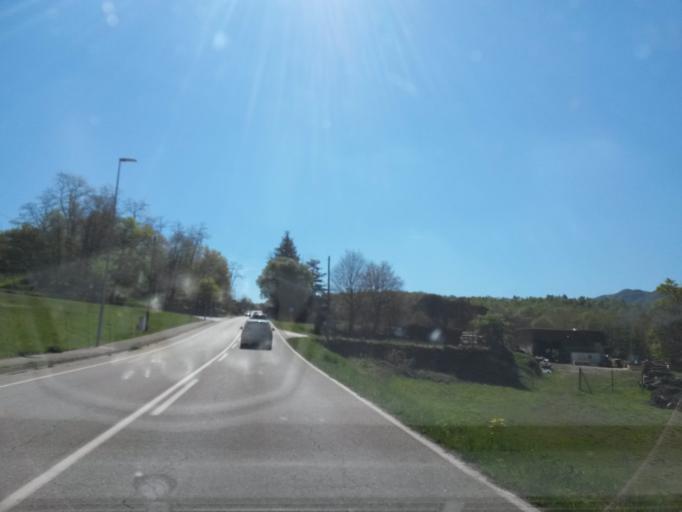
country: ES
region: Catalonia
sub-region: Provincia de Girona
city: Sant Cristofol de les Fonts
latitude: 42.1716
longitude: 2.4982
